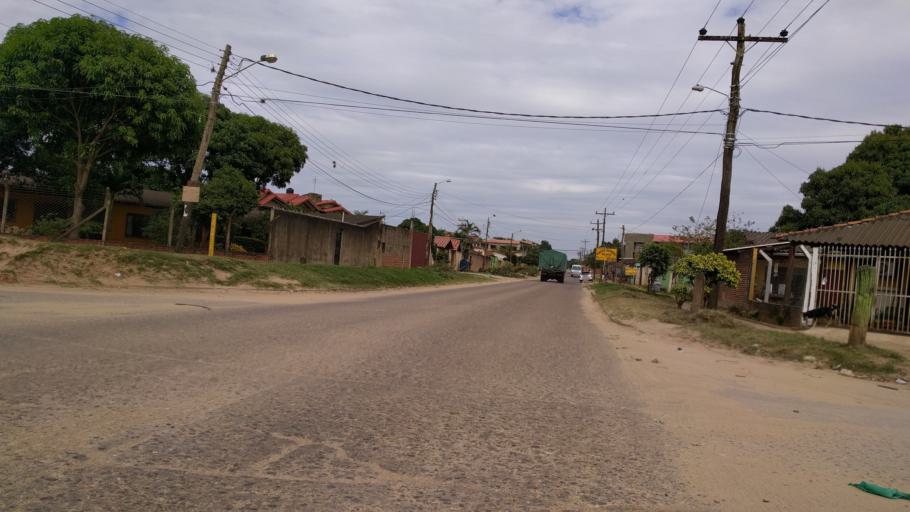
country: BO
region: Santa Cruz
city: Santa Cruz de la Sierra
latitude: -17.8201
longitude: -63.2339
